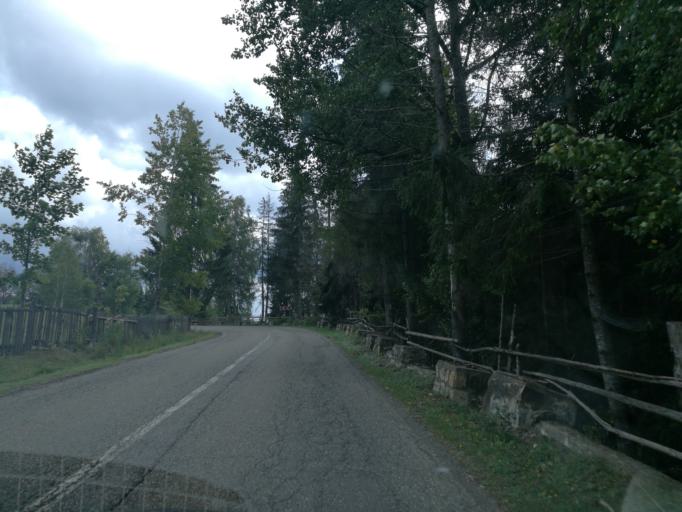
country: RO
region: Suceava
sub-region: Comuna Vatra Moldovitei
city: Vatra Moldovitei
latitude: 47.7284
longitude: 25.6120
